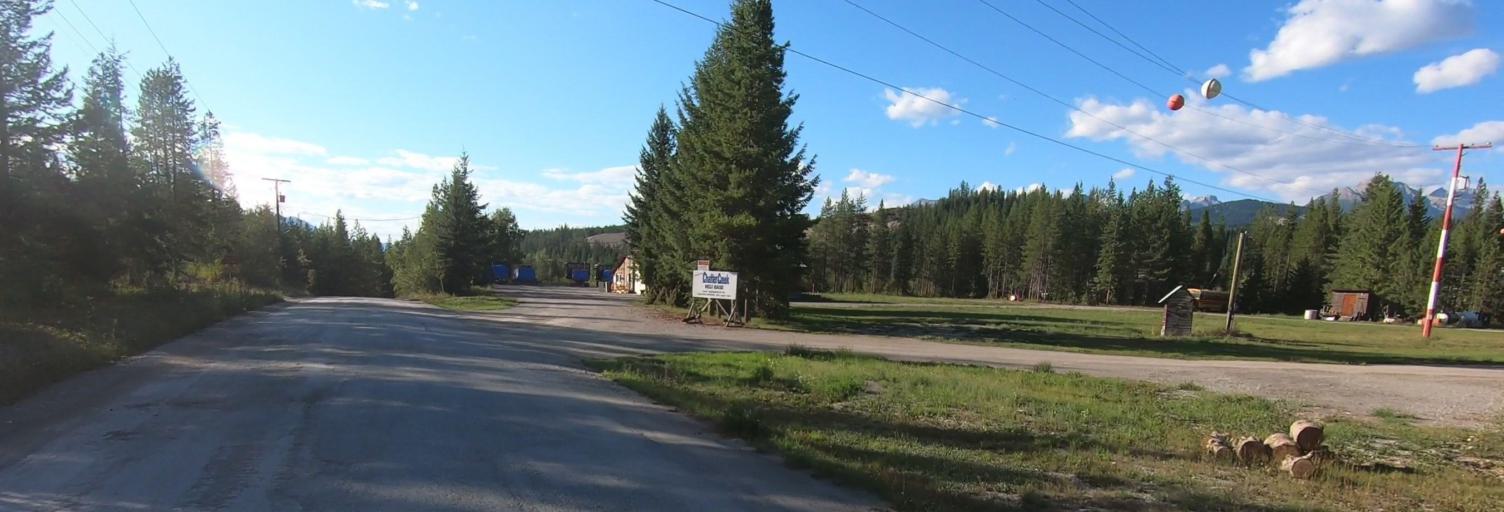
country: CA
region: British Columbia
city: Golden
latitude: 51.4962
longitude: -117.1741
